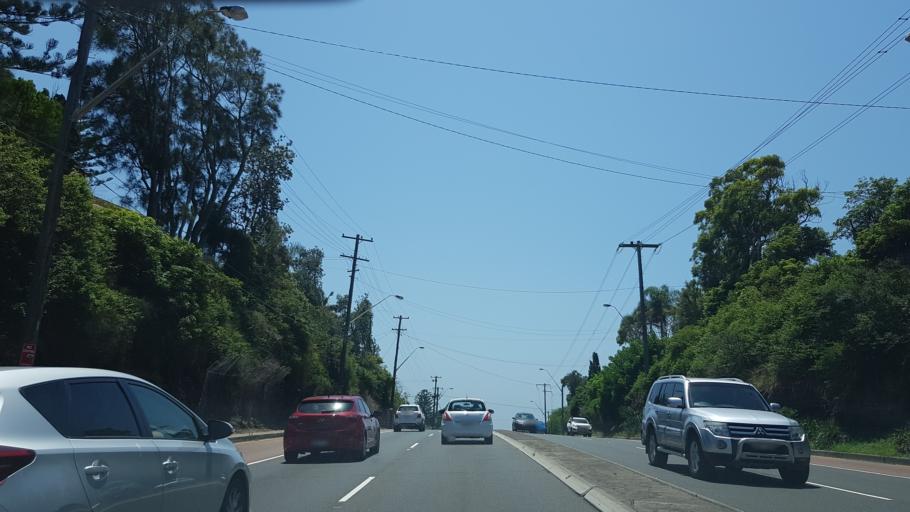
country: AU
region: New South Wales
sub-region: Pittwater
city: Warriewood
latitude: -33.6903
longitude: 151.3051
